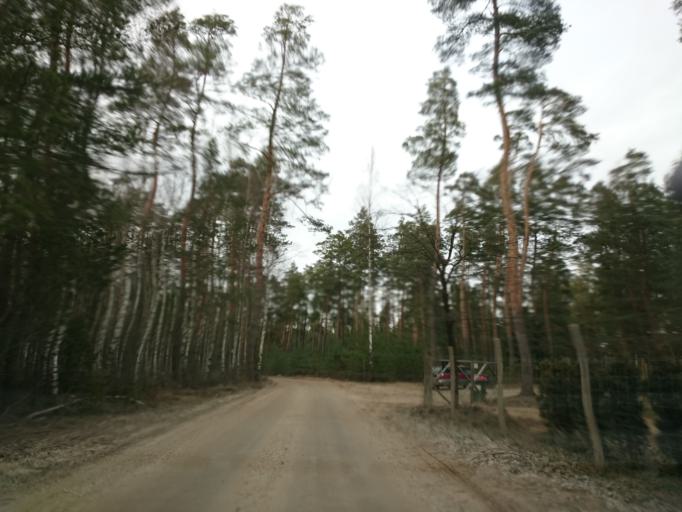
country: LV
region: Garkalne
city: Garkalne
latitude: 57.0255
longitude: 24.3862
